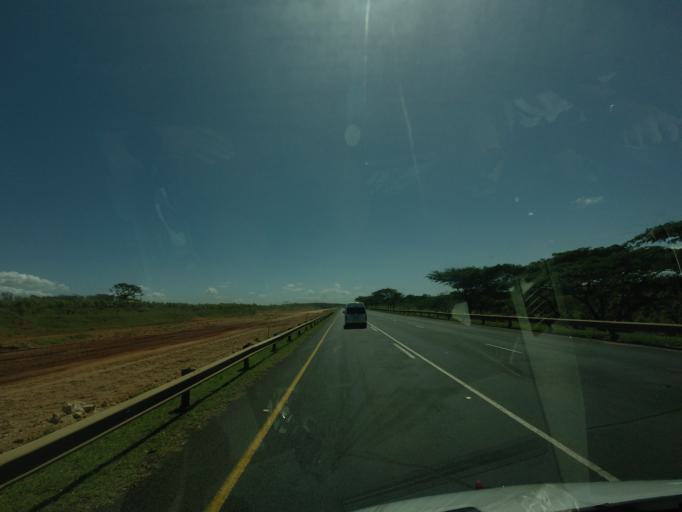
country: ZA
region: KwaZulu-Natal
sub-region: uThungulu District Municipality
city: eSikhawini
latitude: -28.9079
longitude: 31.8173
